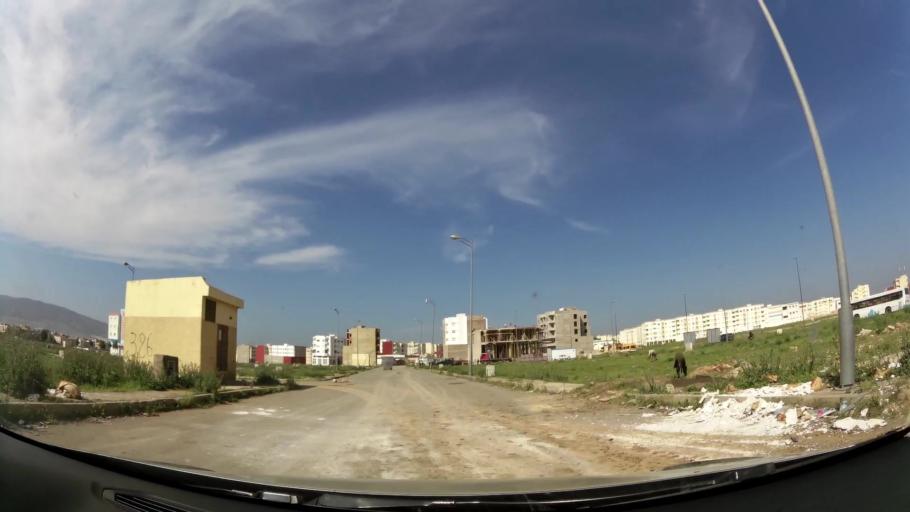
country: MA
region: Fes-Boulemane
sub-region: Fes
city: Fes
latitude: 34.0099
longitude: -5.0457
